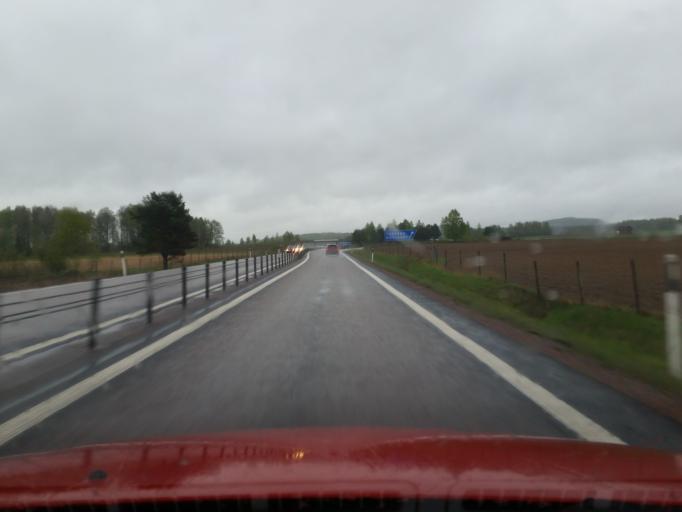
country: SE
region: Dalarna
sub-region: Borlange Kommun
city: Ornas
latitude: 60.4211
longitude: 15.5478
